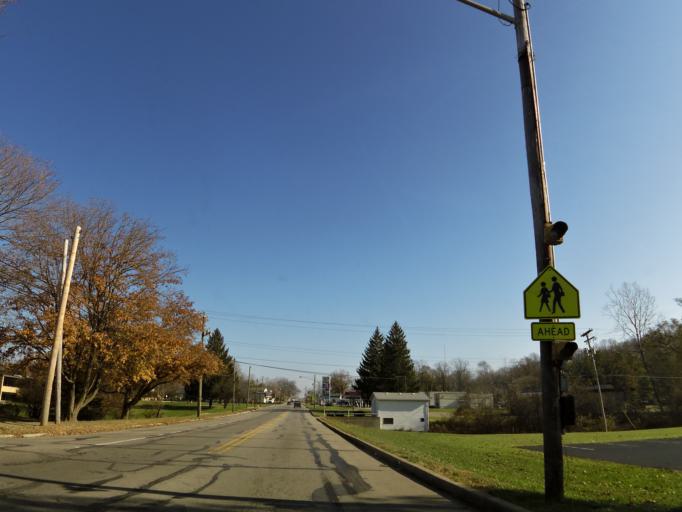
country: US
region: Indiana
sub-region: Fayette County
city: Connersville
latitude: 39.6399
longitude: -85.1513
